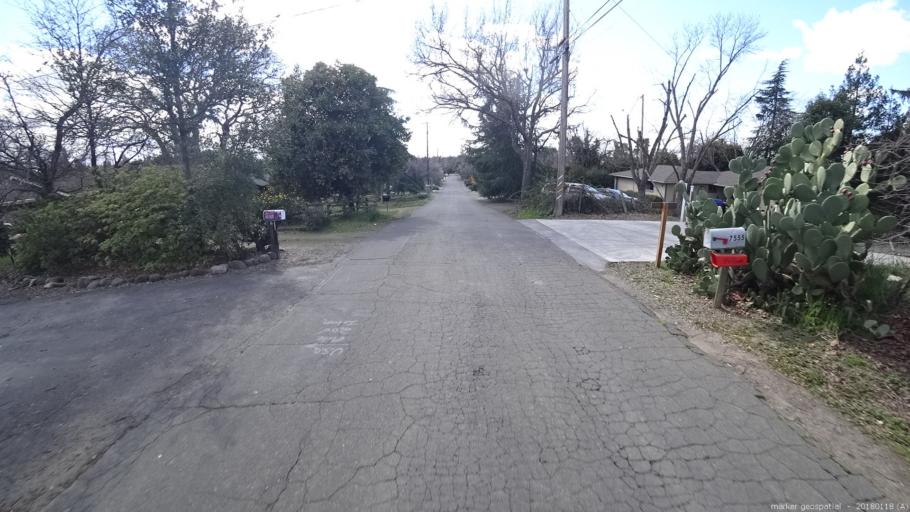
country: US
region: California
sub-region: Sacramento County
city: Folsom
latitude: 38.7028
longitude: -121.1969
